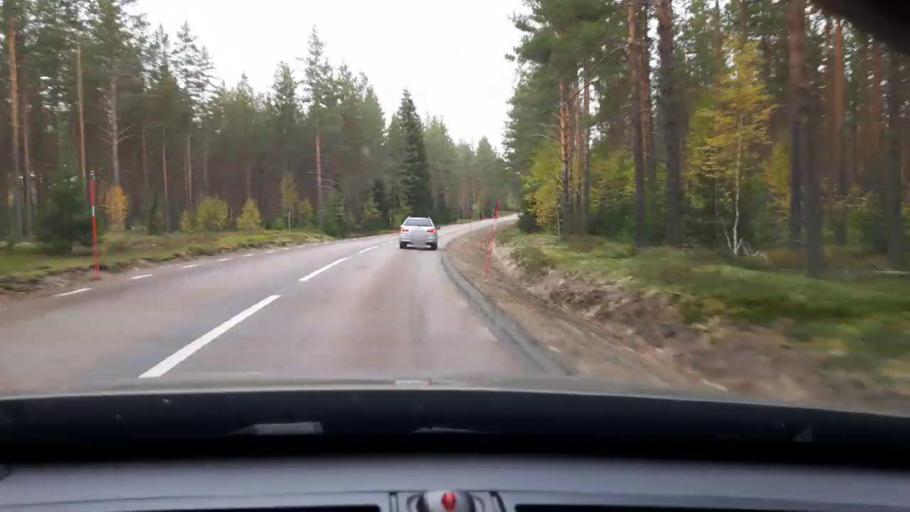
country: SE
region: Dalarna
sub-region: Gagnefs Kommun
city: Mockfjard
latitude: 60.3738
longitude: 14.8080
